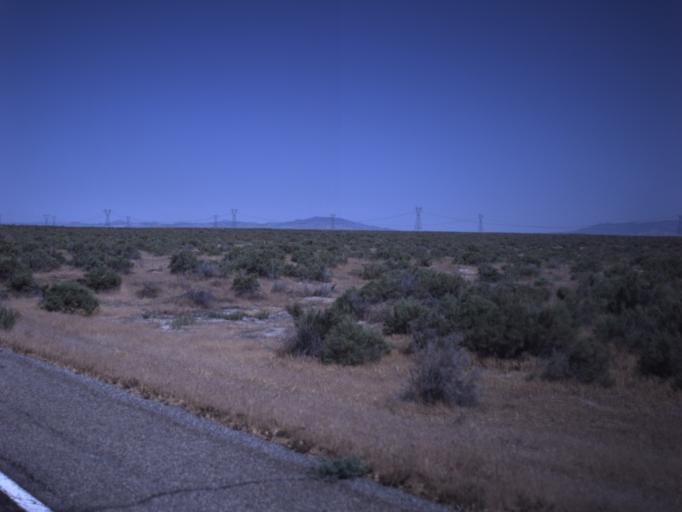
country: US
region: Utah
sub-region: Millard County
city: Delta
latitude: 39.4821
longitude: -112.5173
